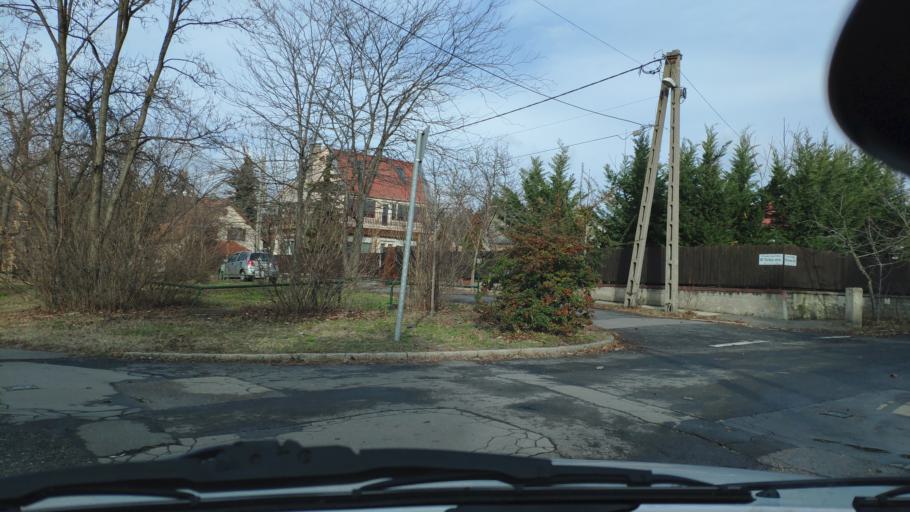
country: HU
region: Budapest
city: Budapest XXI. keruelet
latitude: 47.4101
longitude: 19.0774
